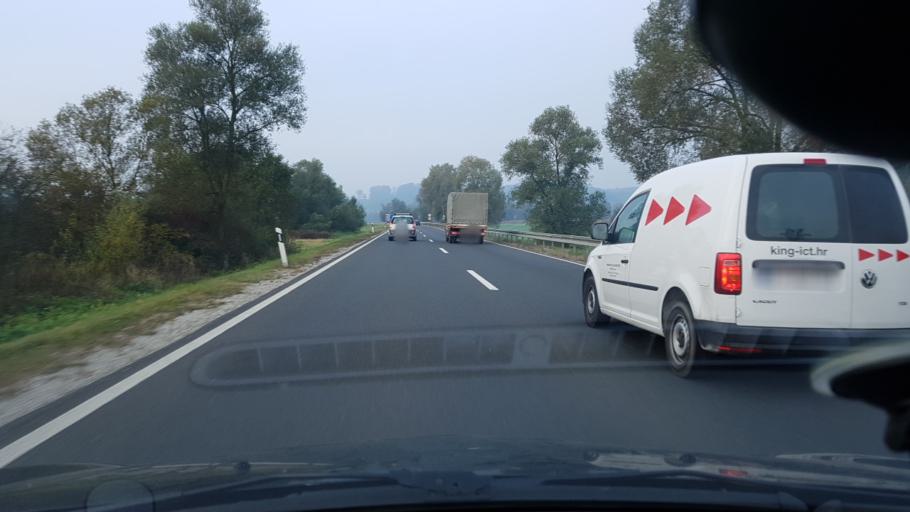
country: HR
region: Zagrebacka
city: Jakovlje
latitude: 45.9891
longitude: 15.8499
